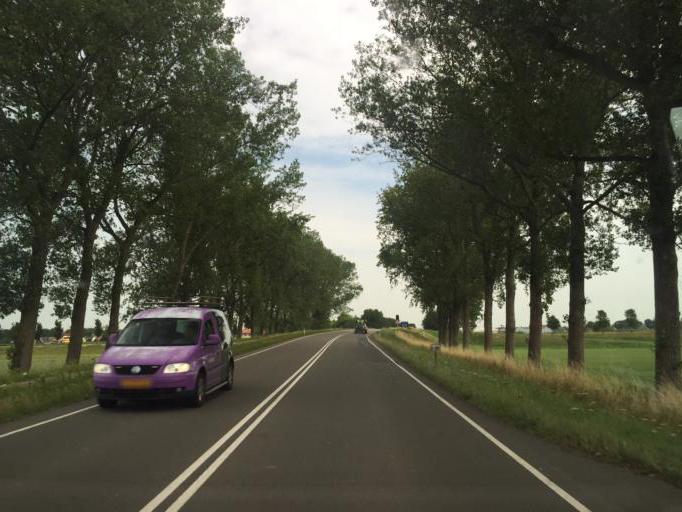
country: NL
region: North Holland
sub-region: Gemeente Beemster
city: Halfweg
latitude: 52.6113
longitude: 4.9520
